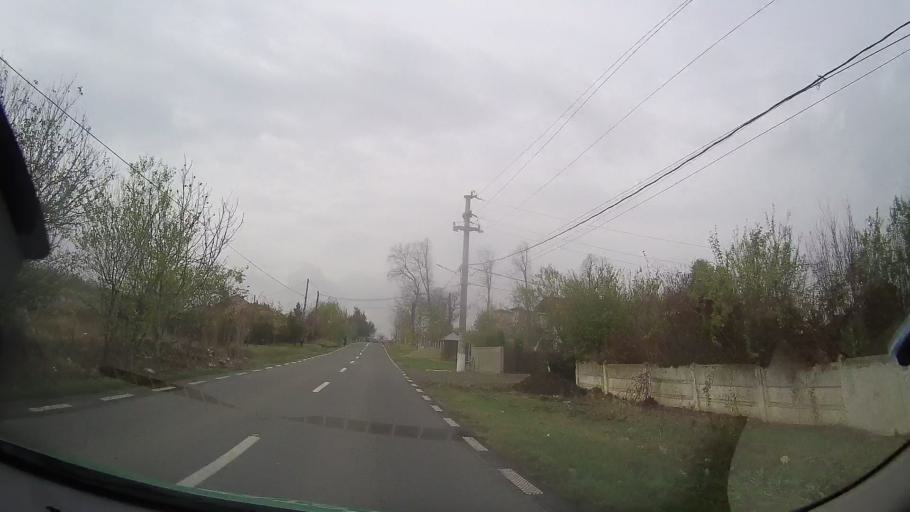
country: RO
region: Ilfov
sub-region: Comuna Gruiu
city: Lipia
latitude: 44.7164
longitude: 26.2506
